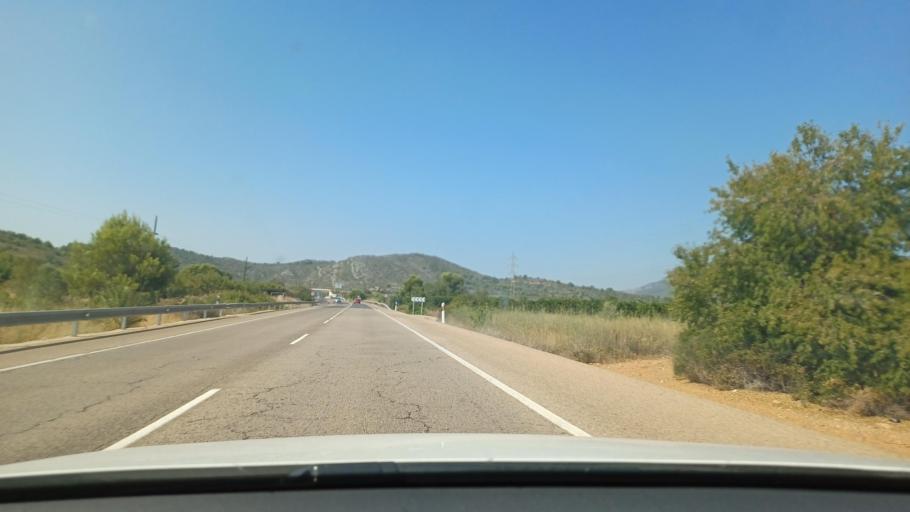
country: ES
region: Valencia
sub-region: Provincia de Castello
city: Alcala de Xivert
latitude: 40.2626
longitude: 0.2394
